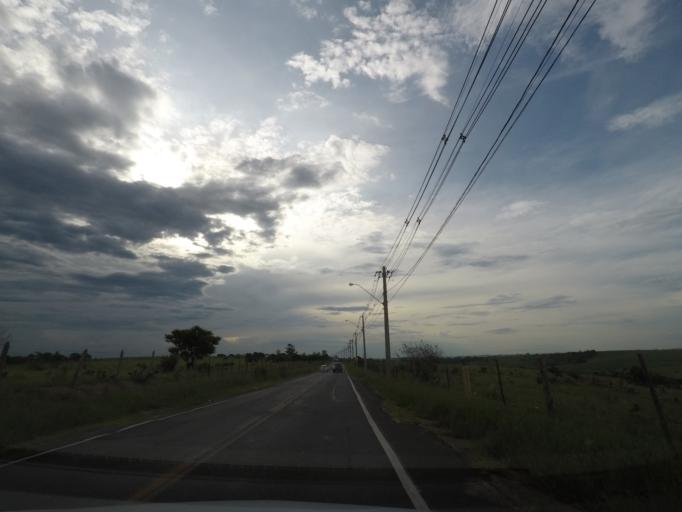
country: BR
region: Sao Paulo
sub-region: Hortolandia
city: Hortolandia
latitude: -22.9577
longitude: -47.2072
